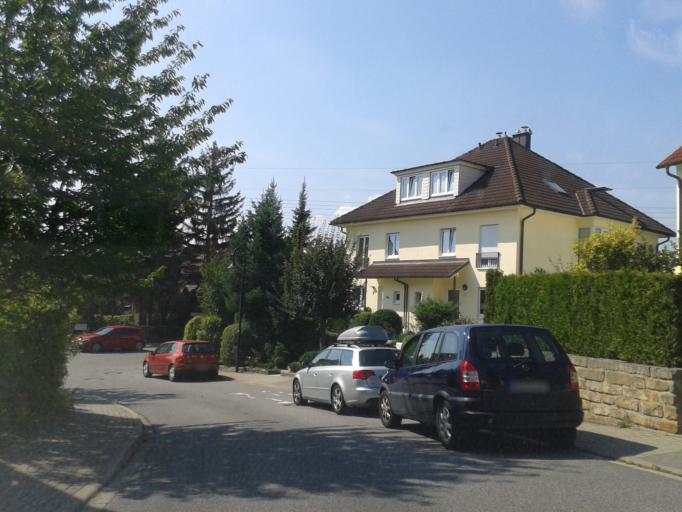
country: DE
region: Saxony
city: Bannewitz
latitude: 51.0174
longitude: 13.7345
